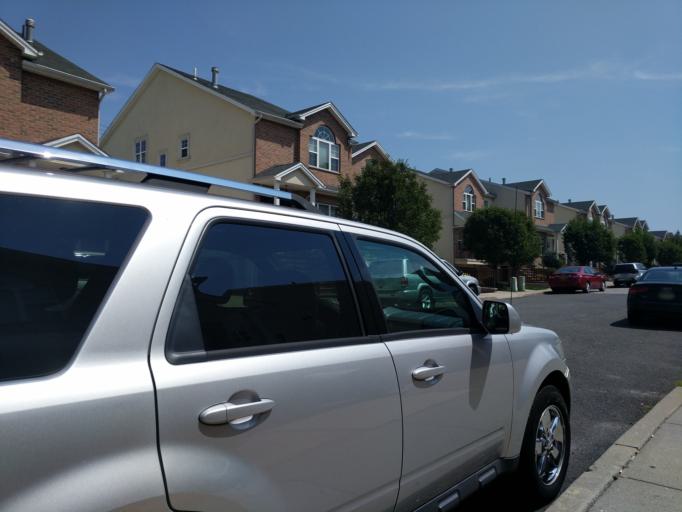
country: US
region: New Jersey
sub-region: Middlesex County
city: Carteret
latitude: 40.5379
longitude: -74.2126
